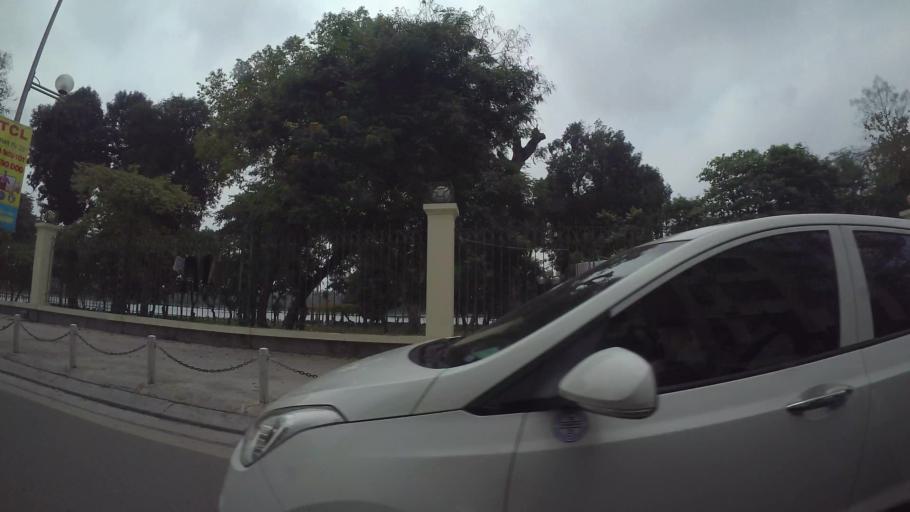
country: VN
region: Ha Noi
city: Hai BaTrung
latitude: 21.0106
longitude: 105.8458
